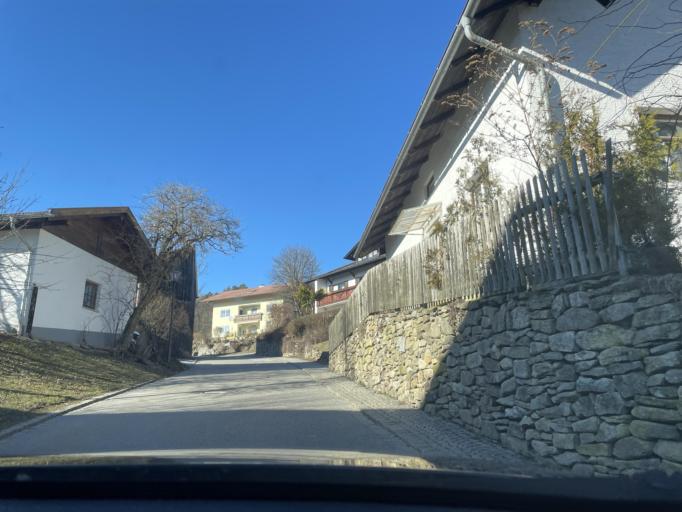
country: DE
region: Bavaria
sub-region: Lower Bavaria
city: Geiersthal
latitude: 49.0721
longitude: 12.9506
